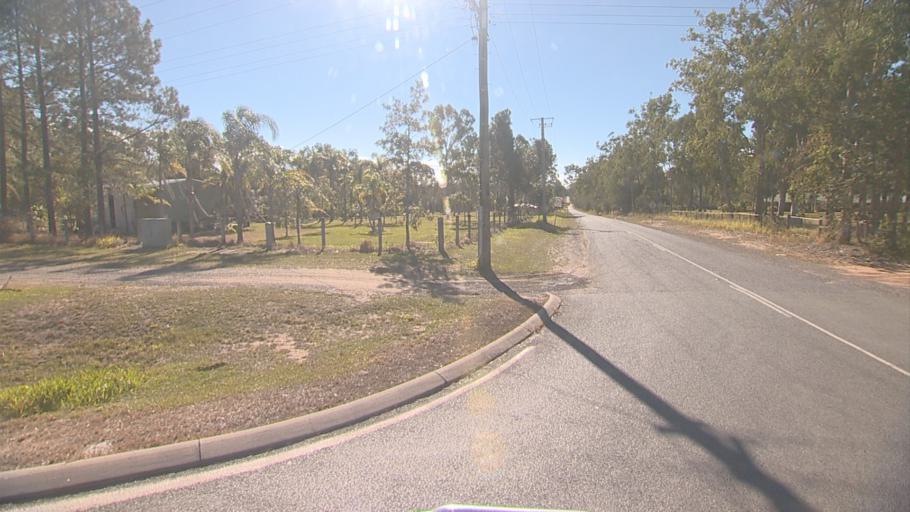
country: AU
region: Queensland
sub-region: Logan
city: Chambers Flat
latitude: -27.8044
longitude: 153.0713
